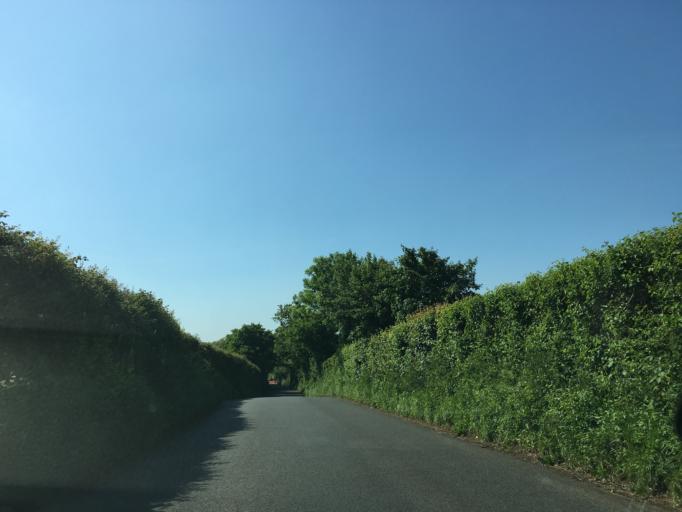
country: GB
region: England
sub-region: Isle of Wight
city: Newchurch
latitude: 50.6737
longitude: -1.2110
